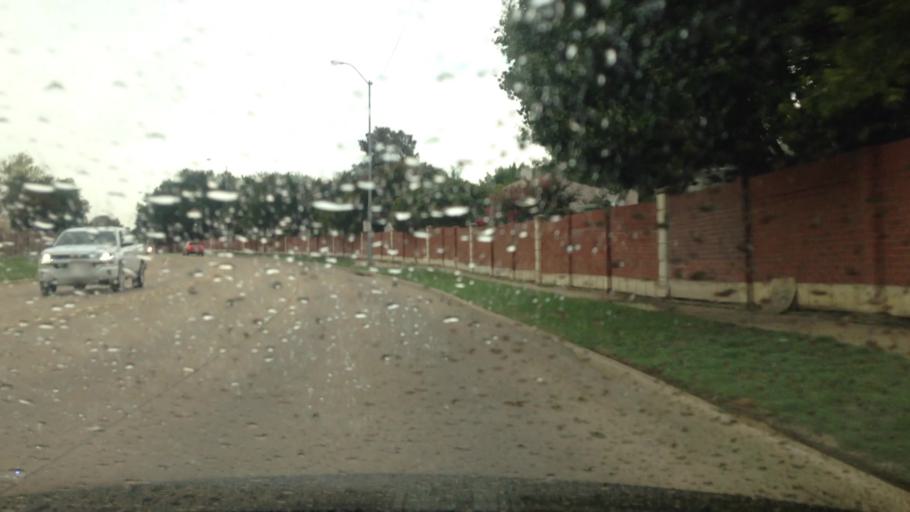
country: US
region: Texas
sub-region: Tarrant County
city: Watauga
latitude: 32.8536
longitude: -97.2765
